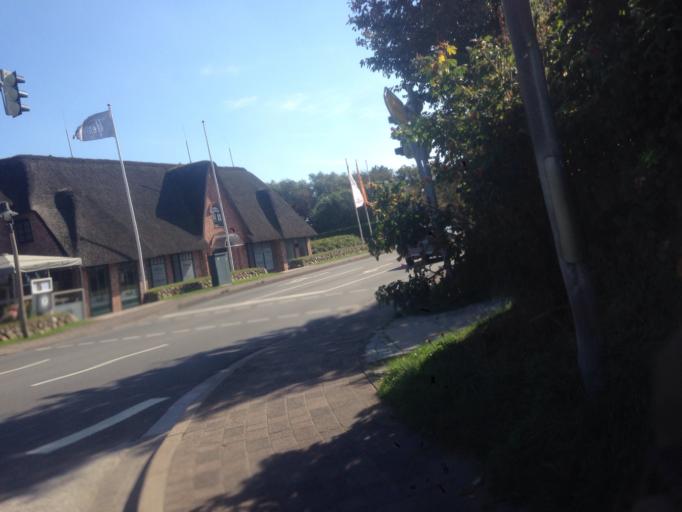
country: DE
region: Schleswig-Holstein
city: Tinnum
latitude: 54.9541
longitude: 8.3422
